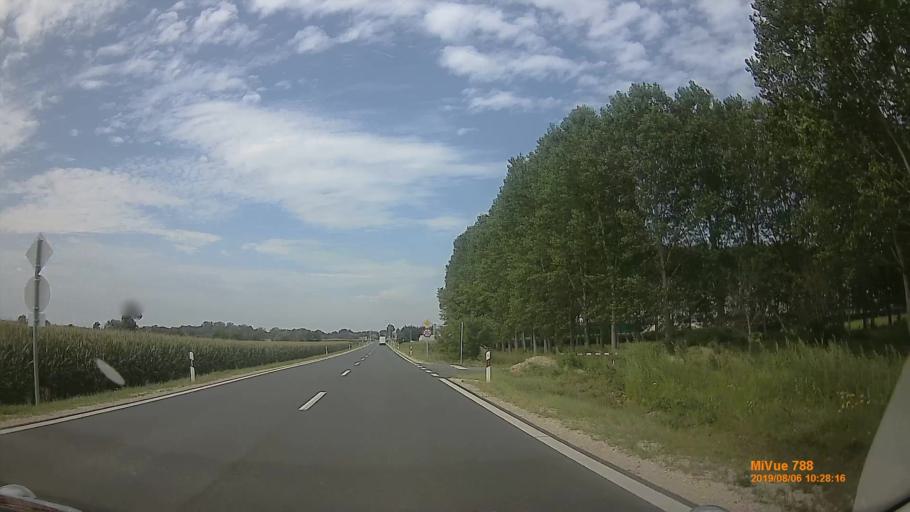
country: HU
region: Vas
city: Kormend
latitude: 47.0368
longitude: 16.6568
